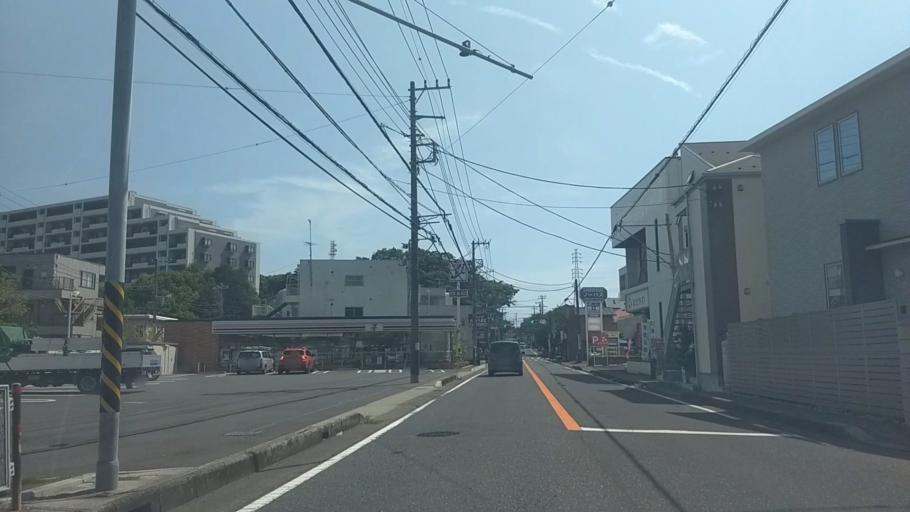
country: JP
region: Kanagawa
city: Kamakura
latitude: 35.3547
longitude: 139.5445
